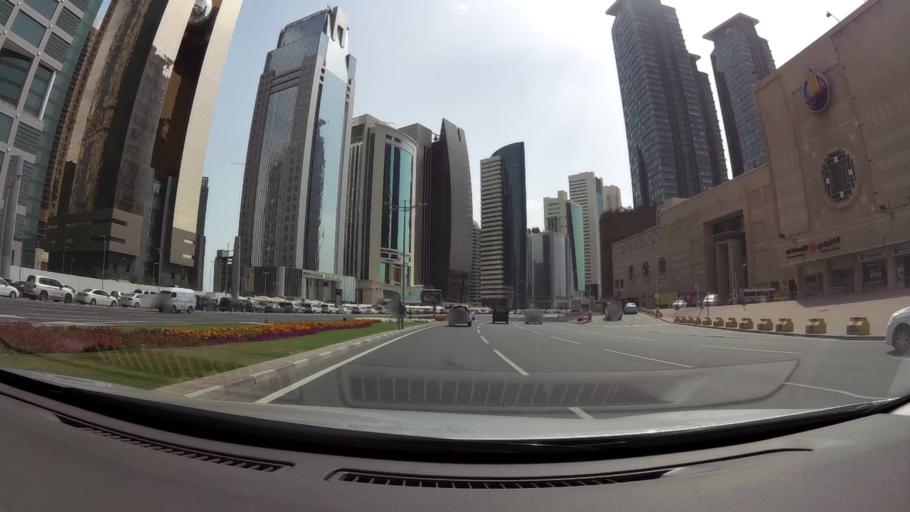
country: QA
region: Baladiyat ad Dawhah
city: Doha
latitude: 25.3261
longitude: 51.5314
